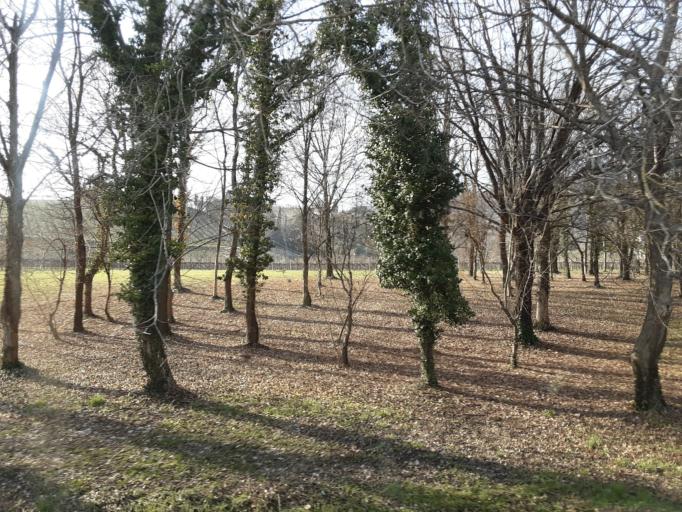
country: IT
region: Veneto
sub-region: Provincia di Treviso
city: Carpesica
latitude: 45.9608
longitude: 12.2840
